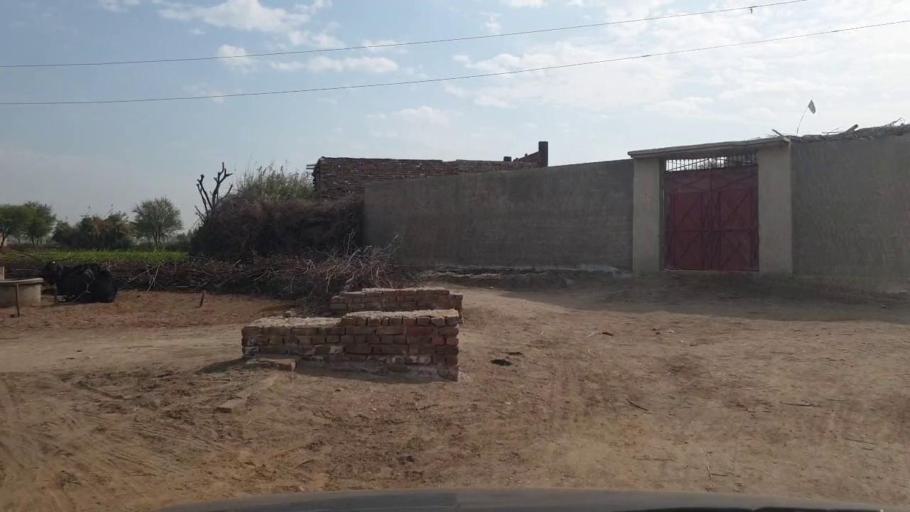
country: PK
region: Sindh
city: Sakrand
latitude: 26.0046
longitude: 68.4017
